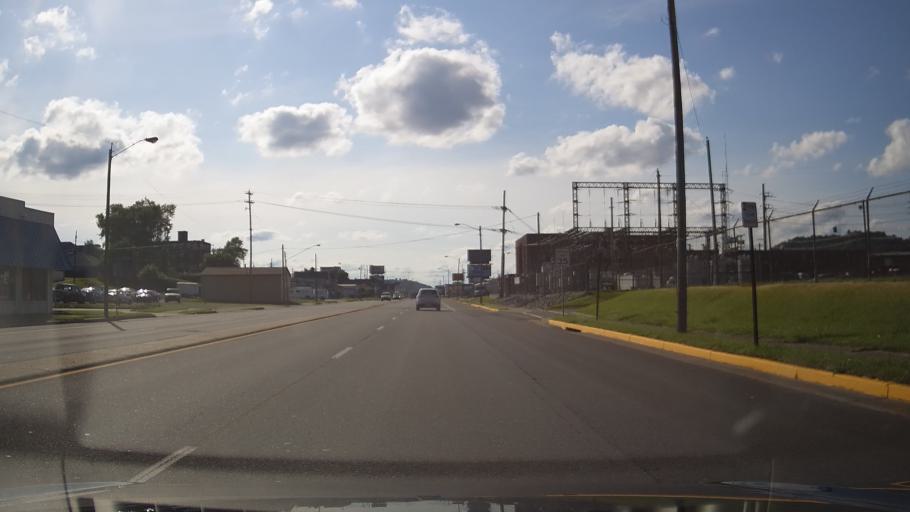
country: US
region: Kentucky
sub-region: Boyd County
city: Ashland
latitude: 38.4735
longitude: -82.6265
